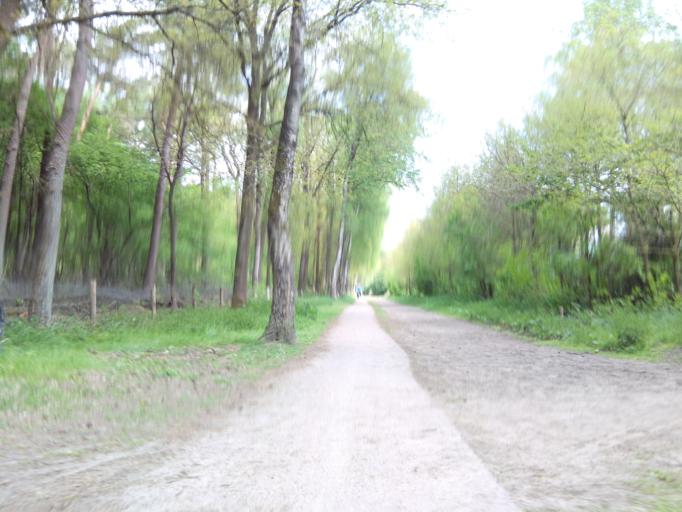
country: NL
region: Gelderland
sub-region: Gemeente Ede
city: Otterlo
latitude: 52.0846
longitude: 5.7641
